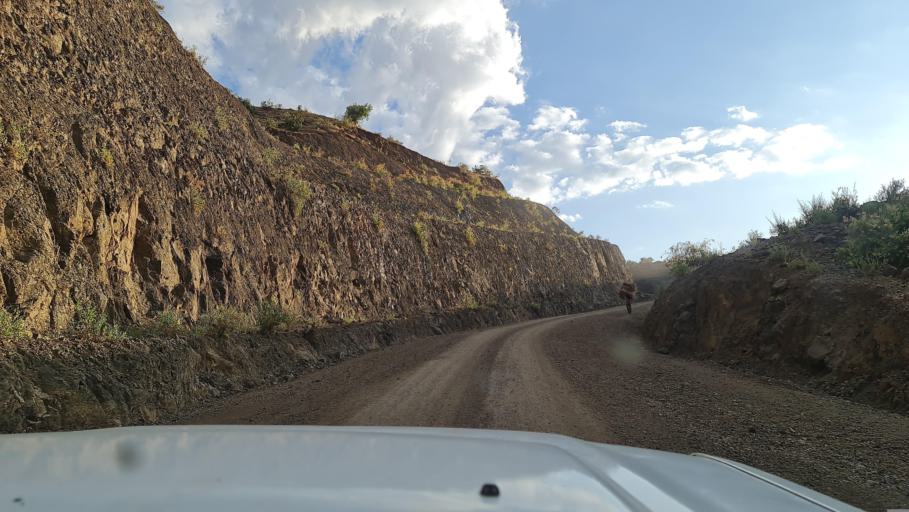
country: ET
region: Amhara
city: Debark'
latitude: 13.0263
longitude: 38.0534
